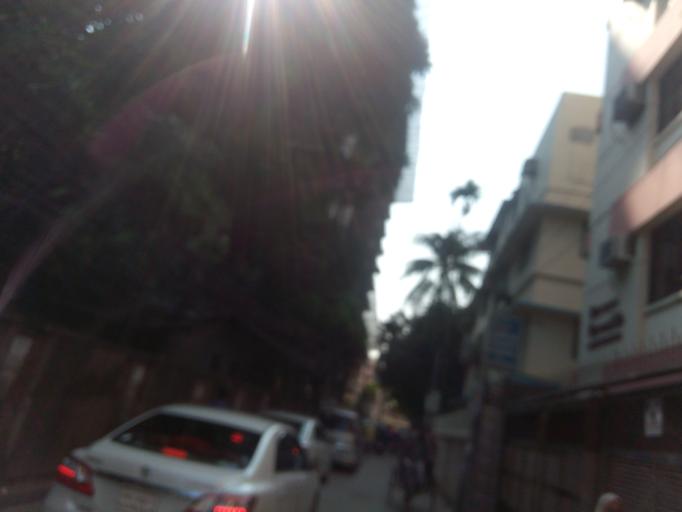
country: BD
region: Dhaka
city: Paltan
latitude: 23.7821
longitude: 90.3996
